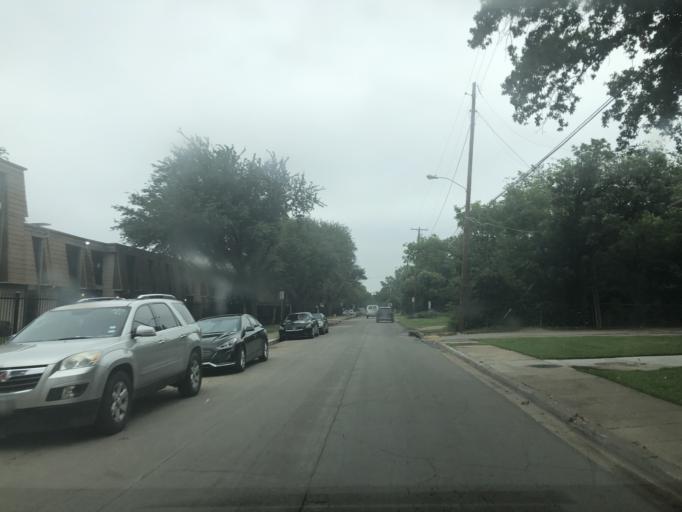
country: US
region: Texas
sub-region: Dallas County
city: Farmers Branch
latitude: 32.8600
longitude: -96.8756
